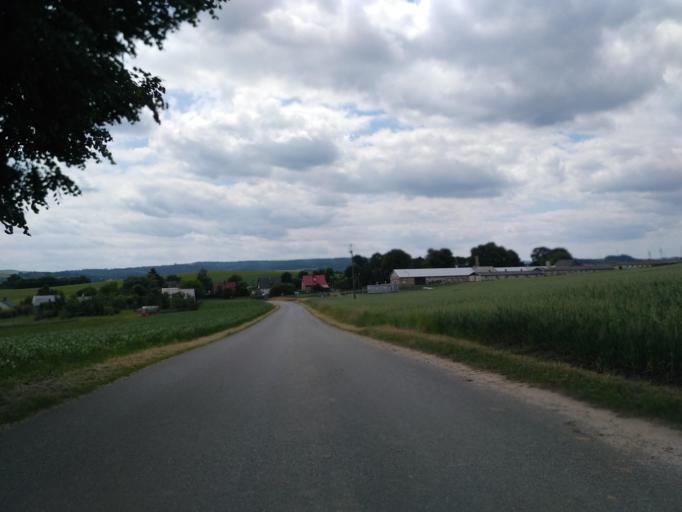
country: PL
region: Subcarpathian Voivodeship
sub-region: Powiat przeworski
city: Jawornik Polski
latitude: 49.8397
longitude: 22.2967
